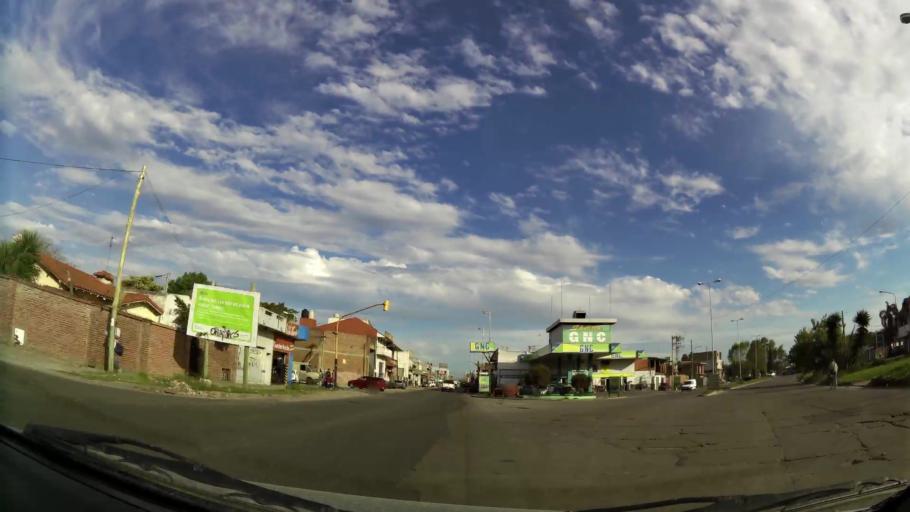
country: AR
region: Buenos Aires
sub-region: Partido de Lanus
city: Lanus
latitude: -34.7108
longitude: -58.3523
